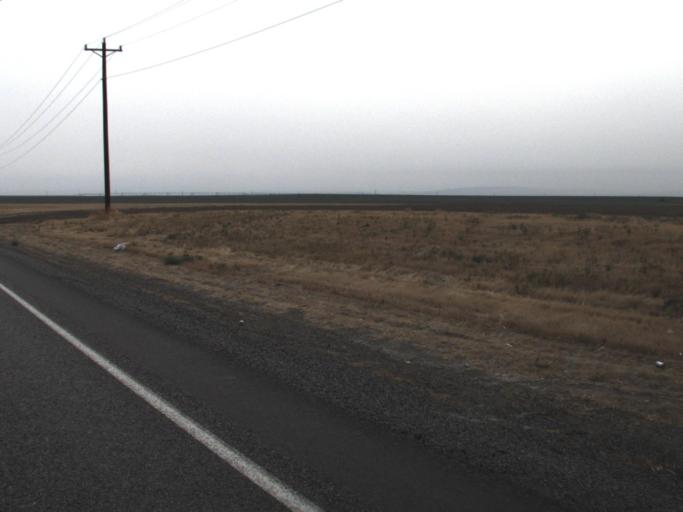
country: US
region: Oregon
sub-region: Morrow County
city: Irrigon
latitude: 46.0557
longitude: -119.6022
